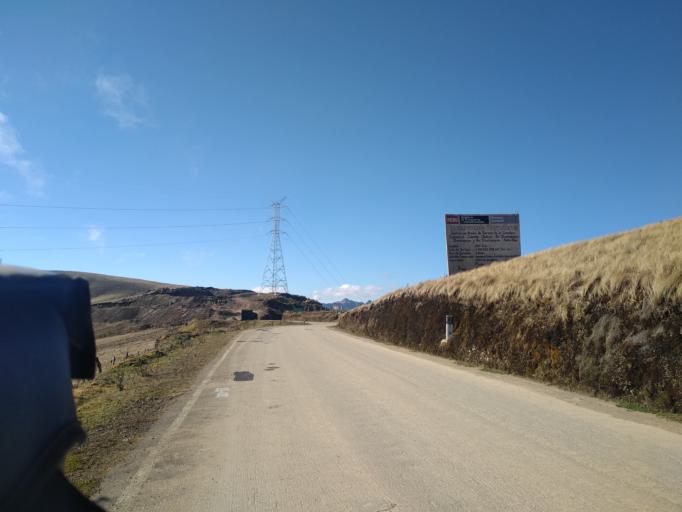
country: PE
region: Amazonas
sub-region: Provincia de Chachapoyas
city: Montevideo
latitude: -6.7321
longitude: -77.8946
